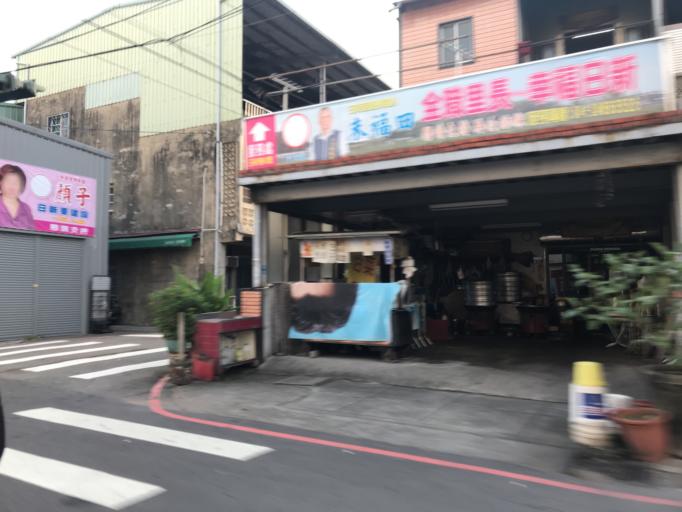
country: TW
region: Taiwan
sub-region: Taichung City
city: Taichung
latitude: 24.1198
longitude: 120.6925
